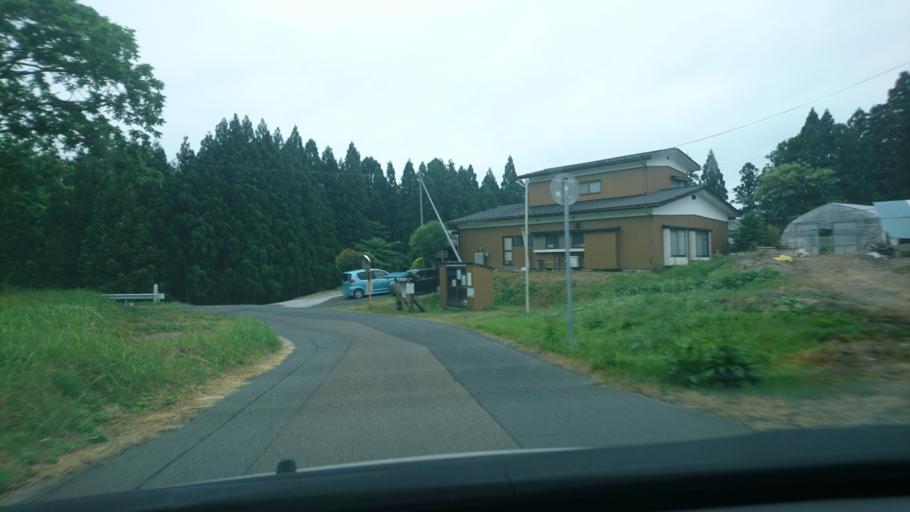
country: JP
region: Iwate
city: Ichinoseki
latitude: 38.9241
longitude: 141.0982
